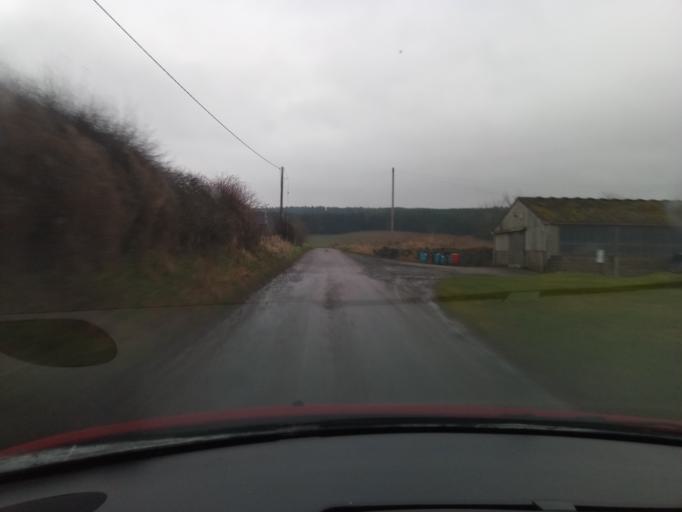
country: GB
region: Scotland
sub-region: The Scottish Borders
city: Kelso
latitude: 55.5399
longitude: -2.4411
